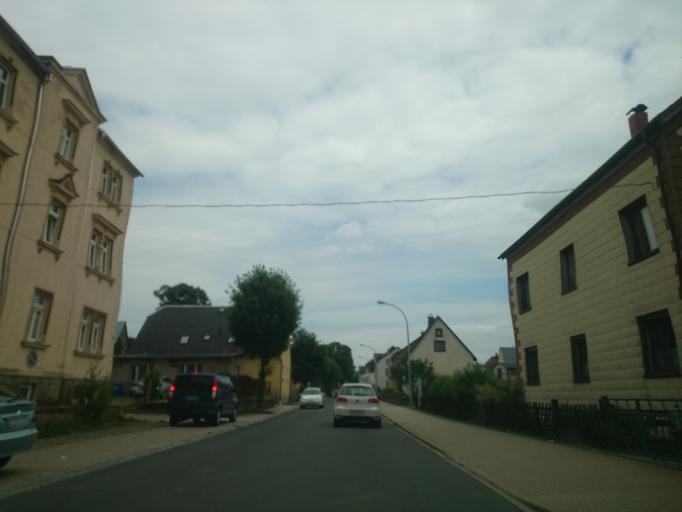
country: DE
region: Saxony
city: Eppendorf
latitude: 50.8023
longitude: 13.2351
